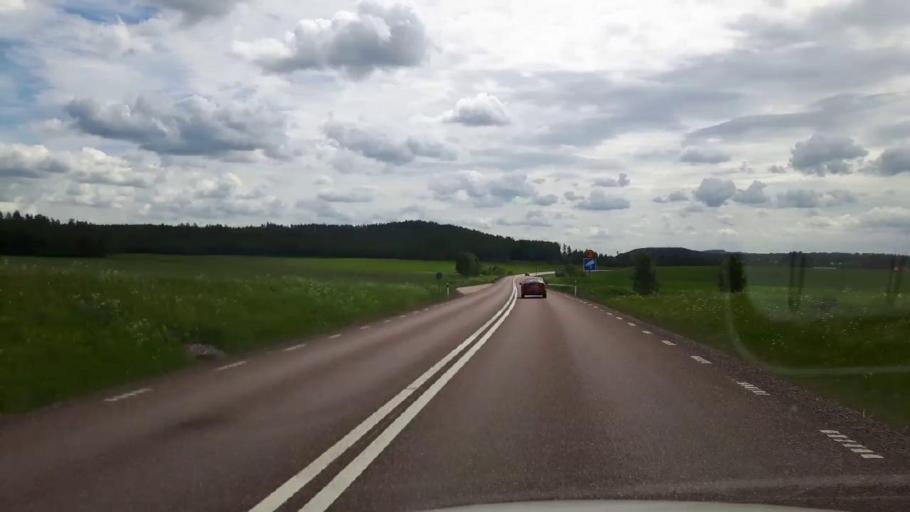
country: SE
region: Dalarna
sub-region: Hedemora Kommun
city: Hedemora
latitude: 60.3333
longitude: 15.9462
